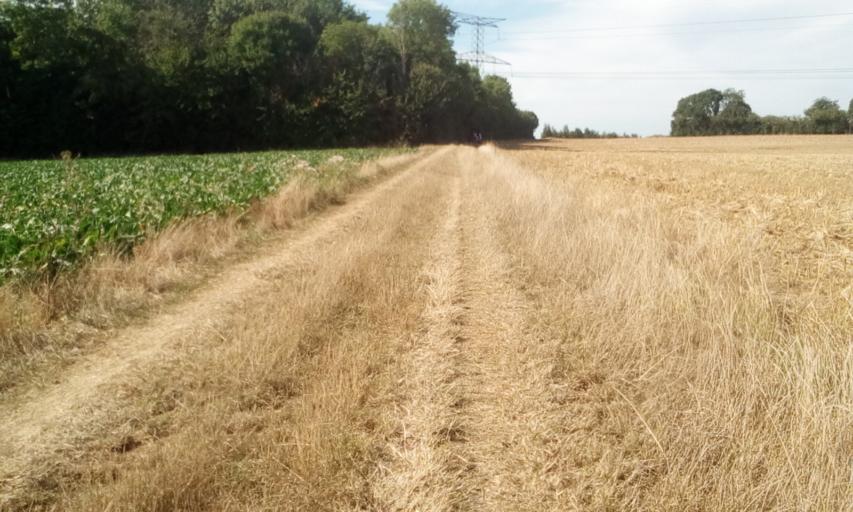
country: FR
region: Lower Normandy
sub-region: Departement du Calvados
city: Fontaine-Etoupefour
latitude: 49.1176
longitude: -0.4568
